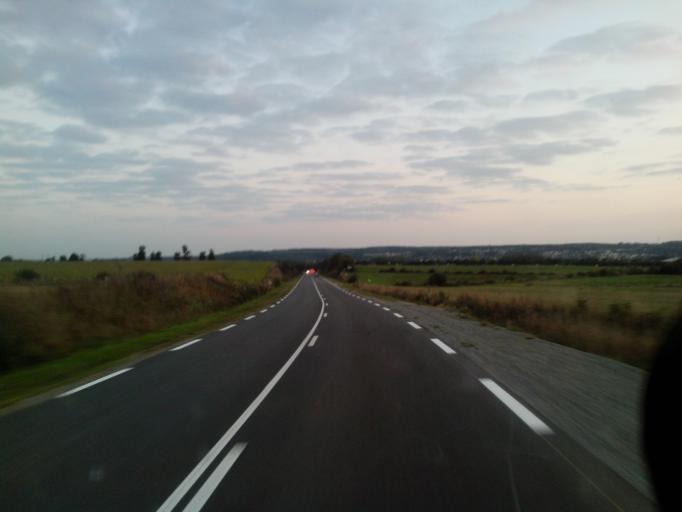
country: FR
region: Brittany
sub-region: Departement d'Ille-et-Vilaine
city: Montfort-sur-Meu
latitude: 48.1565
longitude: -1.9470
